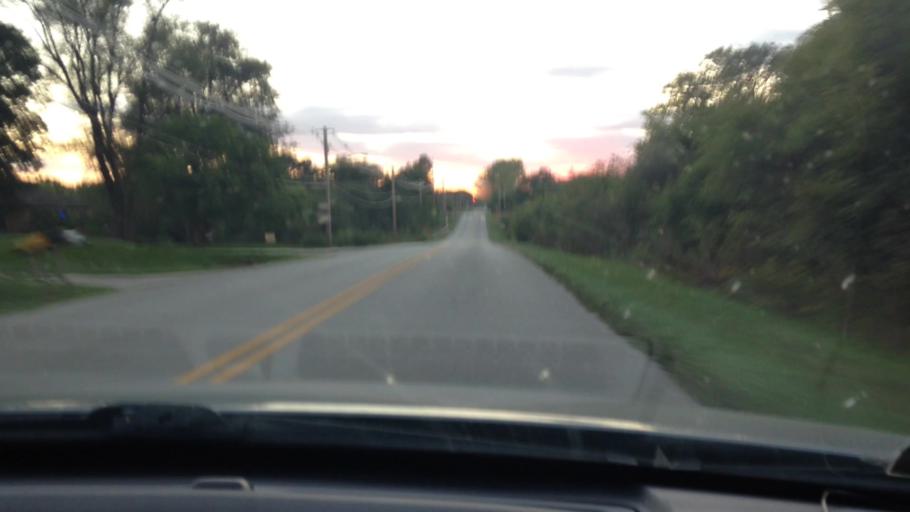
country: US
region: Kansas
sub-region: Leavenworth County
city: Lansing
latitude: 39.1868
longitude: -94.8600
